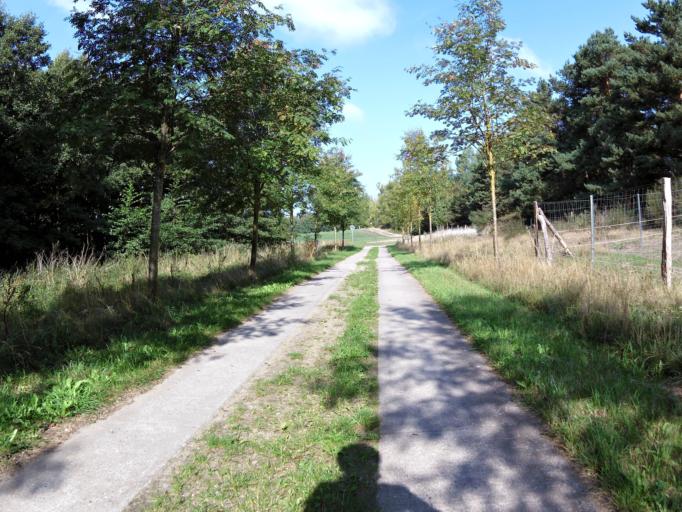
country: DE
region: Mecklenburg-Vorpommern
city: Loddin
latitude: 53.9510
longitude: 14.0401
